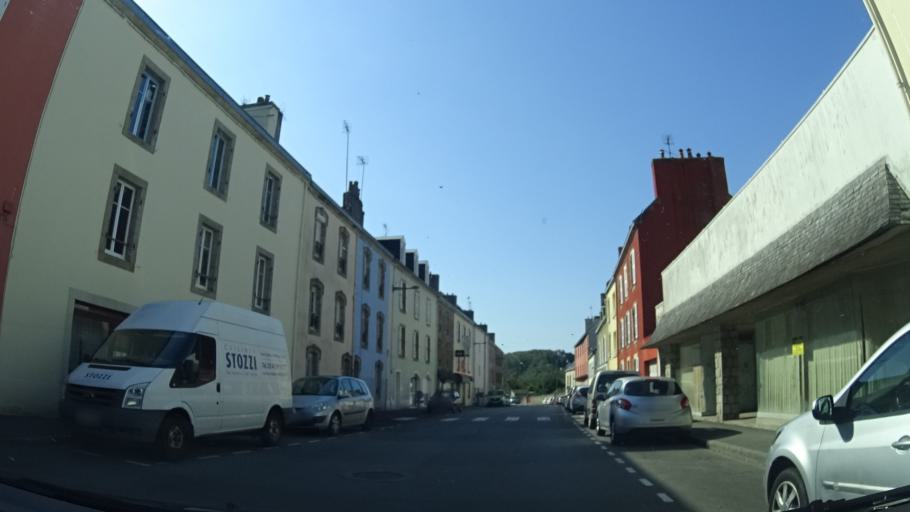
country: FR
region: Brittany
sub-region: Departement du Finistere
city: Douarnenez
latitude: 48.0879
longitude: -4.3294
